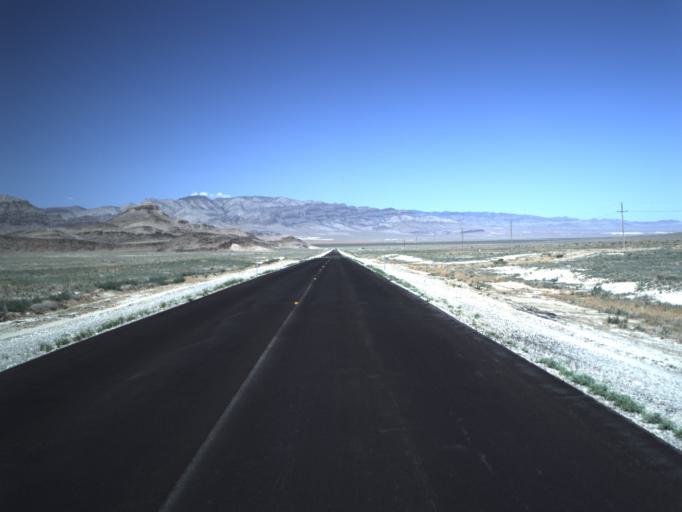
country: US
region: Utah
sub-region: Beaver County
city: Milford
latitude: 39.0491
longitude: -113.4166
